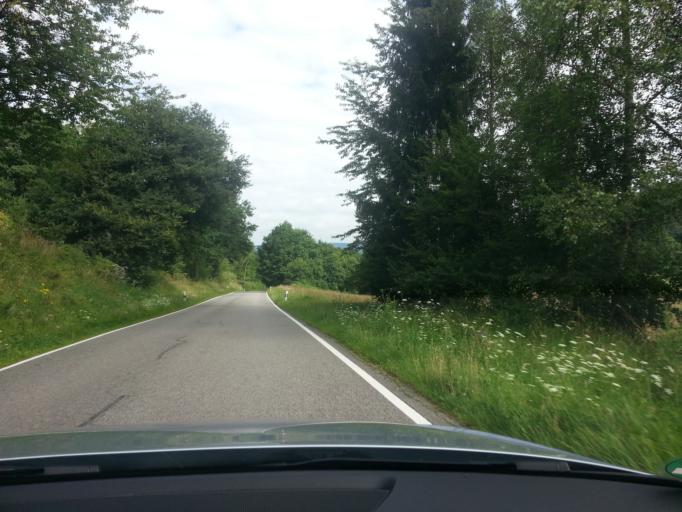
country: DE
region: Saarland
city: Losheim
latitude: 49.4751
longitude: 6.7907
